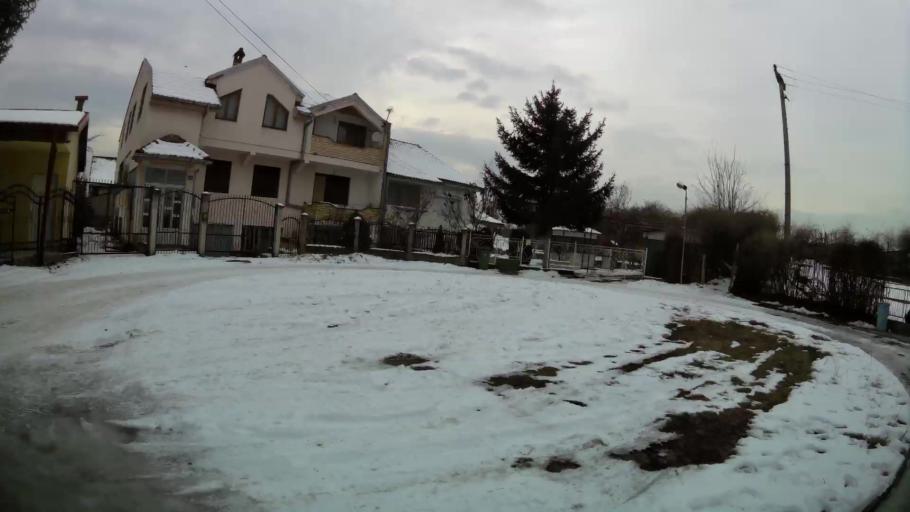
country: MK
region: Butel
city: Butel
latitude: 42.0345
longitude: 21.4422
